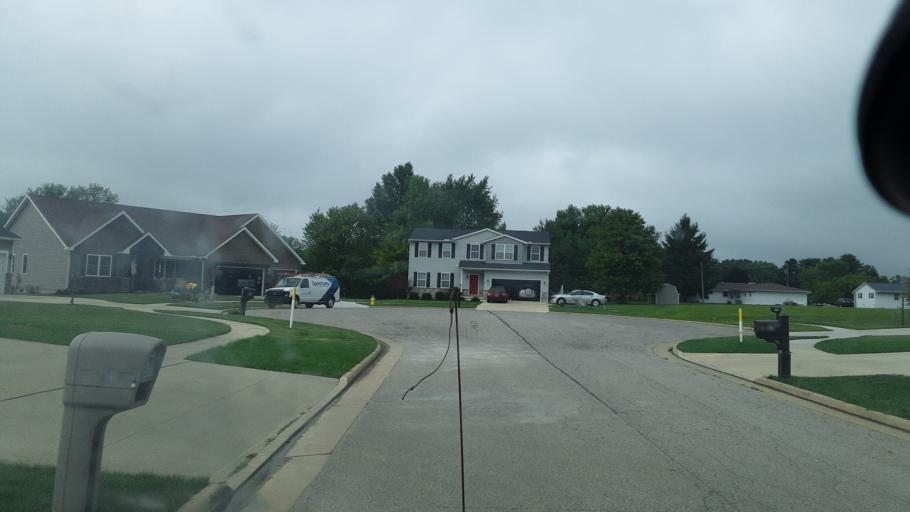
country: US
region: Ohio
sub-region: Richland County
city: Ontario
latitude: 40.7723
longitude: -82.6459
